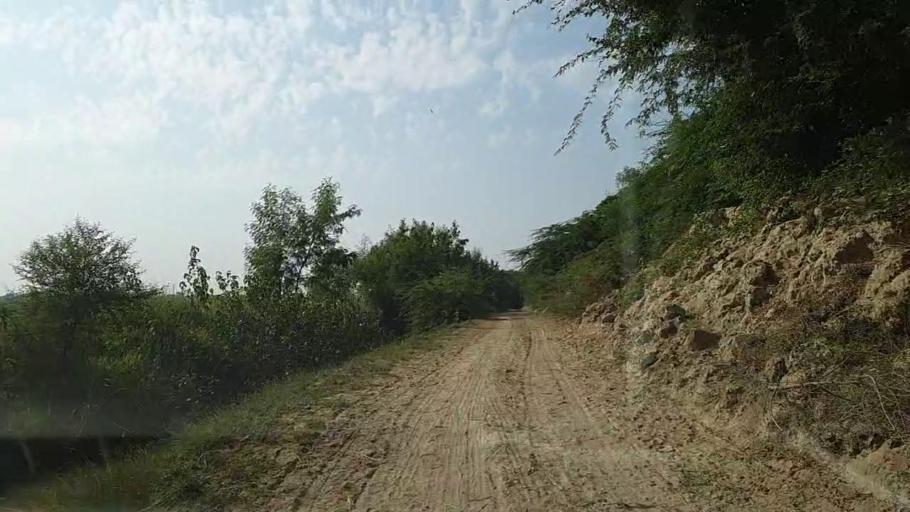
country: PK
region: Sindh
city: Mirpur Batoro
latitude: 24.7071
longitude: 68.3018
